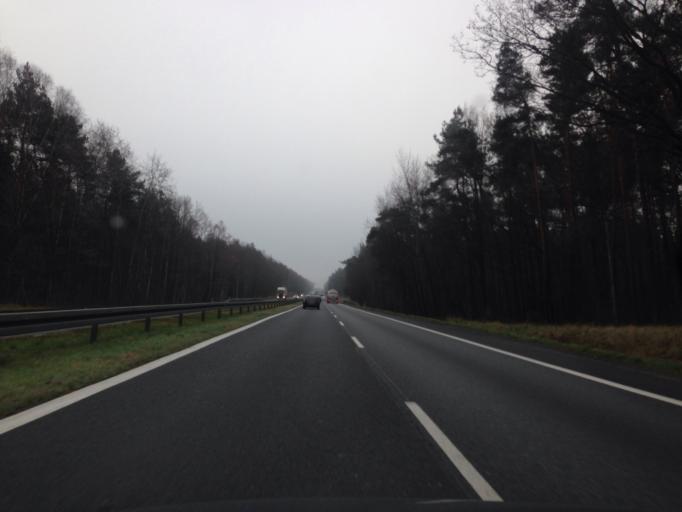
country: PL
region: Silesian Voivodeship
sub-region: Powiat czestochowski
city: Kamienica Polska
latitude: 50.6559
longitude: 19.1312
